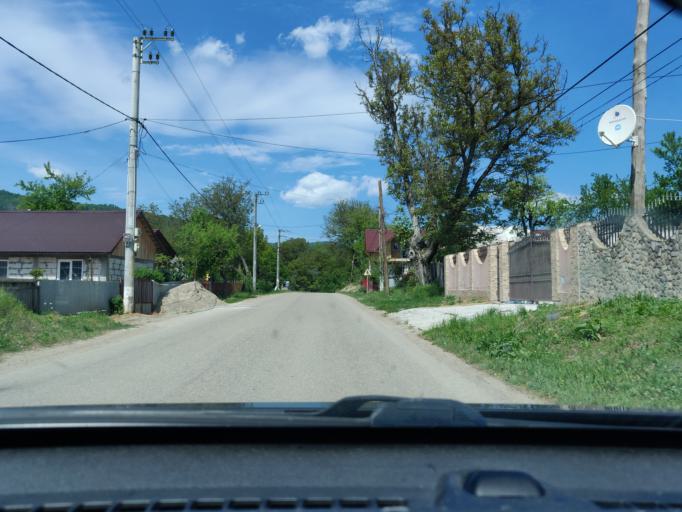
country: RO
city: Vizantea-Manastireasca
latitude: 45.9794
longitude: 26.8004
